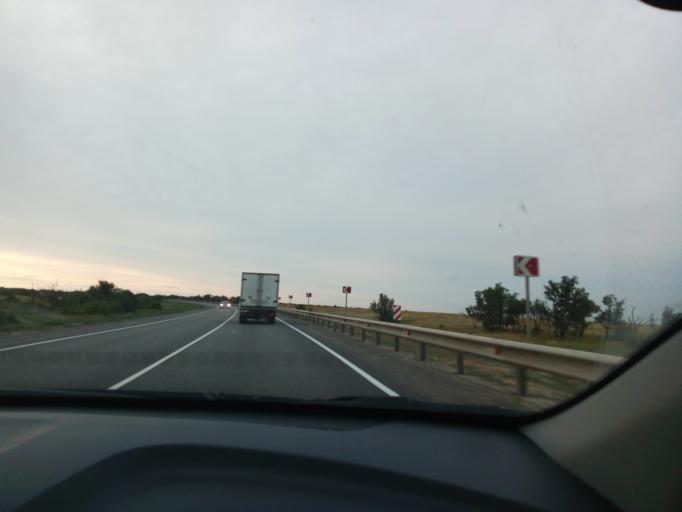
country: RU
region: Volgograd
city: Primorsk
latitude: 49.2186
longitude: 44.9070
